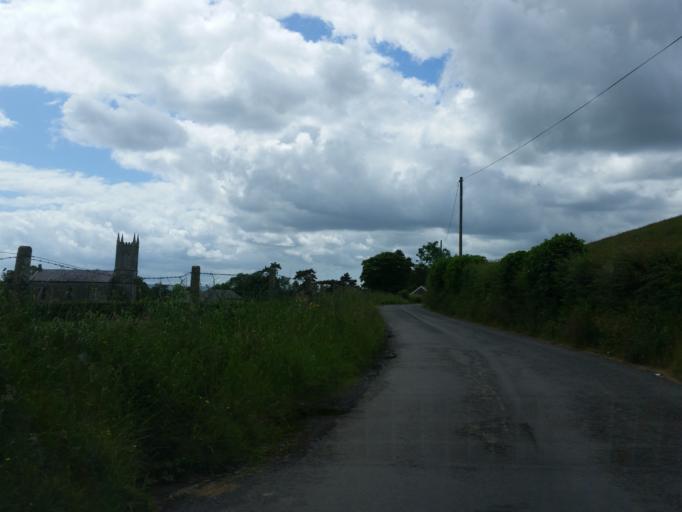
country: IE
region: Ulster
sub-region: County Monaghan
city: Monaghan
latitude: 54.4597
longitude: -7.0750
